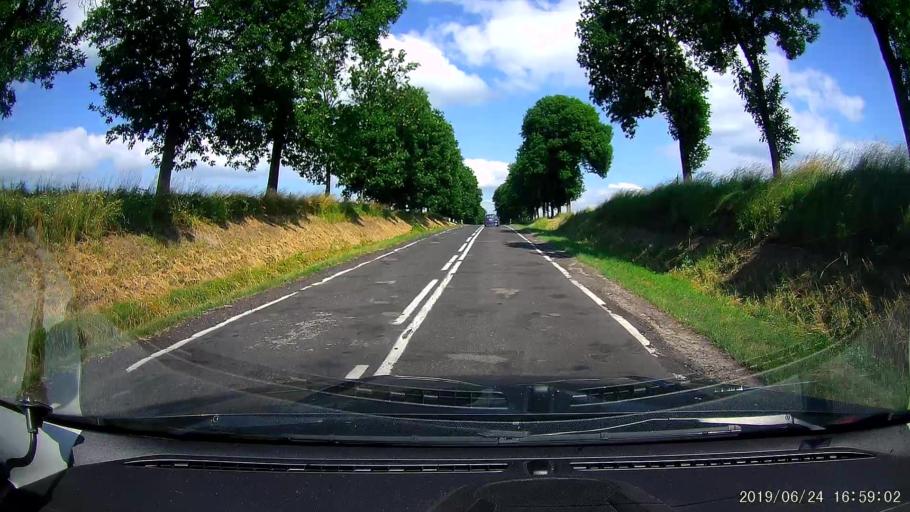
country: PL
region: Lublin Voivodeship
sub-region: Powiat tomaszowski
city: Telatyn
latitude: 50.5241
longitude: 23.8941
